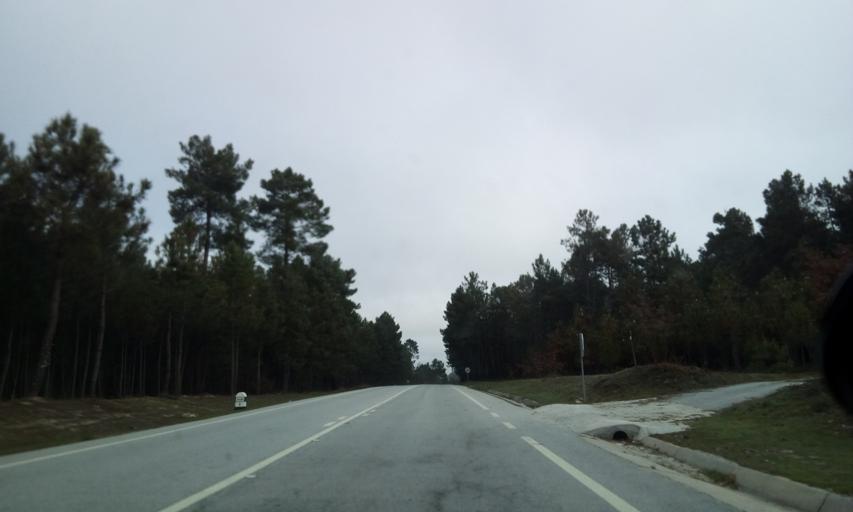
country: PT
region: Guarda
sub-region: Aguiar da Beira
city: Aguiar da Beira
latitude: 40.7521
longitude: -7.5048
